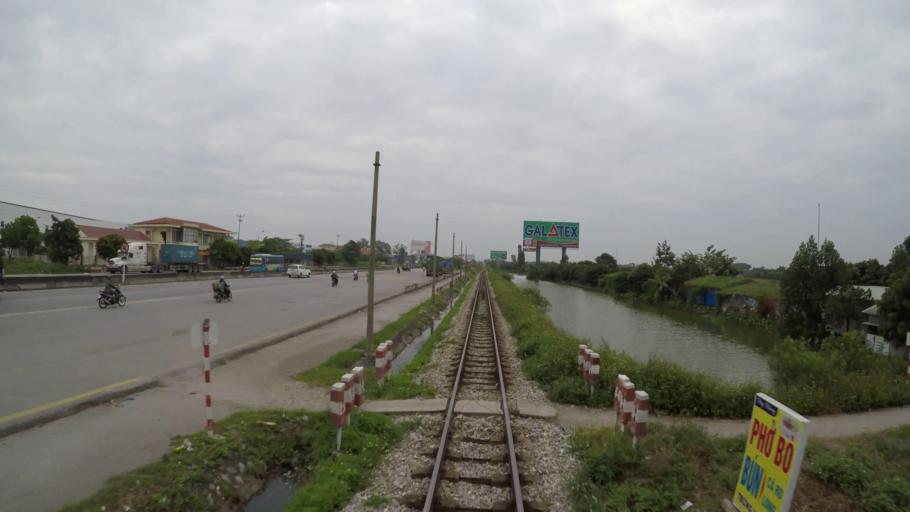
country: VN
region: Hai Duong
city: Nam Sach
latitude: 20.9694
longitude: 106.3810
